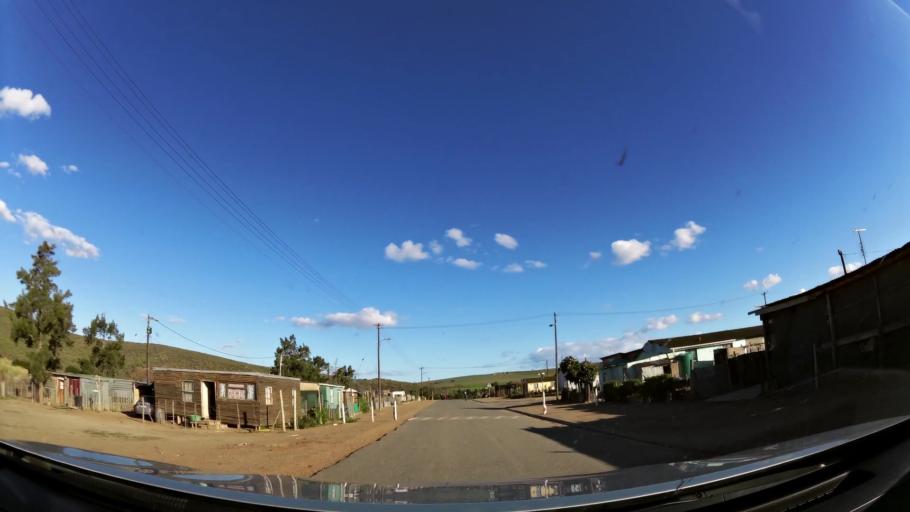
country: ZA
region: Western Cape
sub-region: Eden District Municipality
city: Riversdale
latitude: -34.1049
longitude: 20.9698
